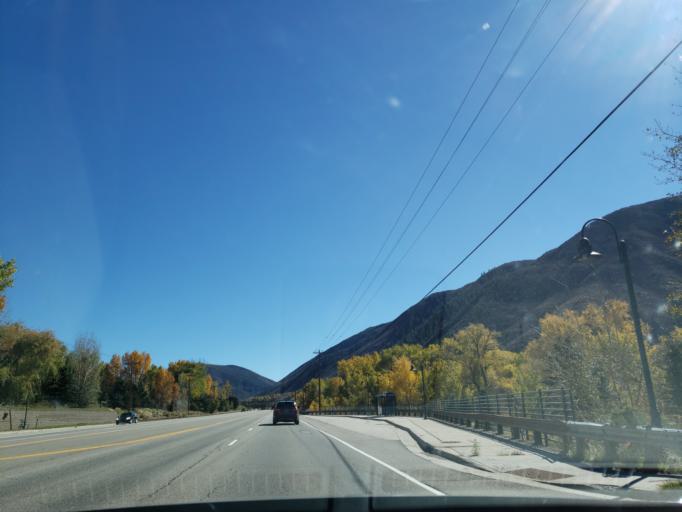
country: US
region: Colorado
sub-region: Eagle County
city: Basalt
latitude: 39.3508
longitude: -107.0169
